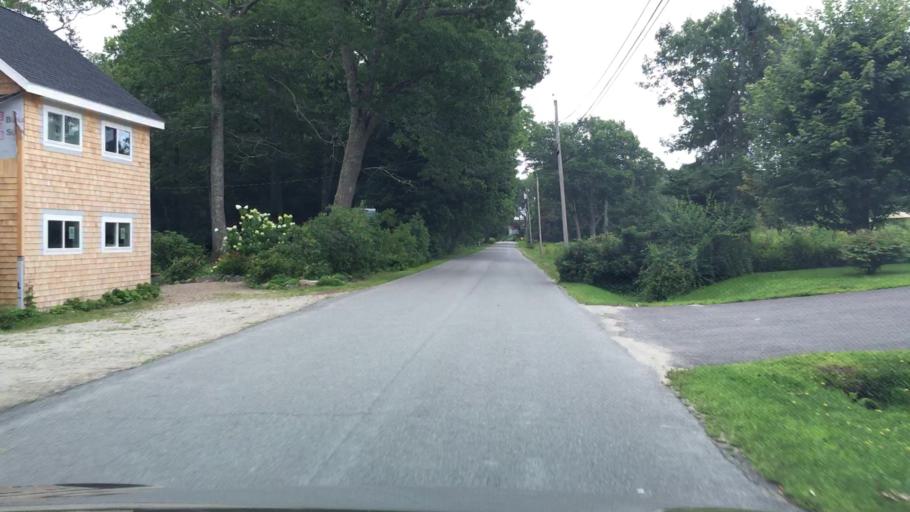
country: US
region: Maine
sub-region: Waldo County
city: Stockton Springs
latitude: 44.5114
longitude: -68.8106
